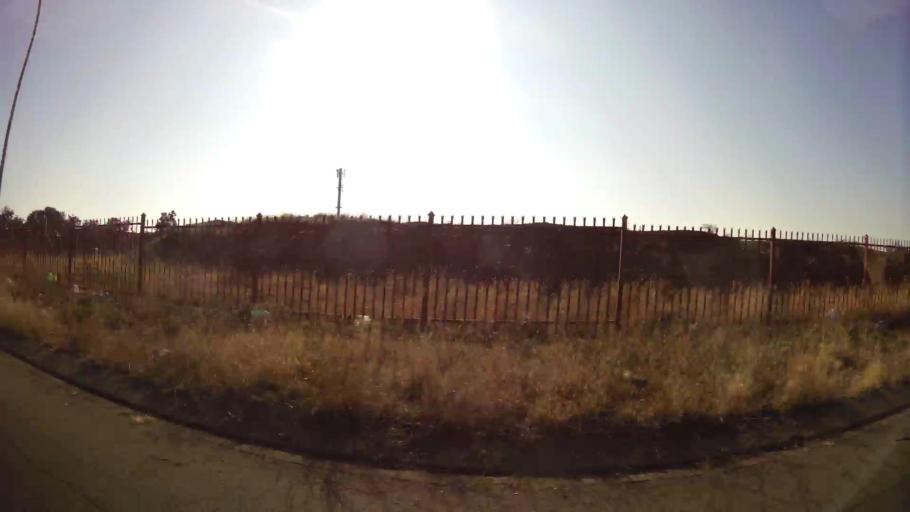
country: ZA
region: Orange Free State
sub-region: Mangaung Metropolitan Municipality
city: Bloemfontein
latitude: -29.1823
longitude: 26.1699
